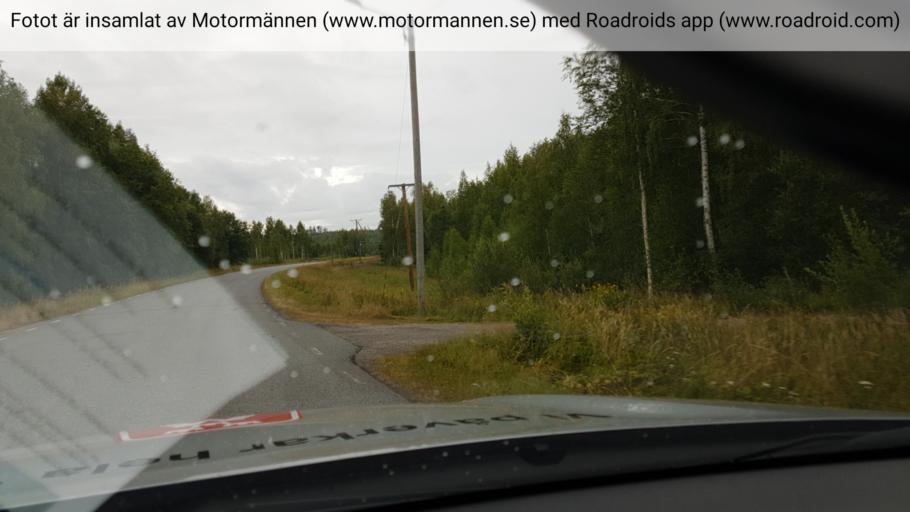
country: SE
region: Norrbotten
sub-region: Bodens Kommun
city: Boden
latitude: 65.8241
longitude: 21.5333
